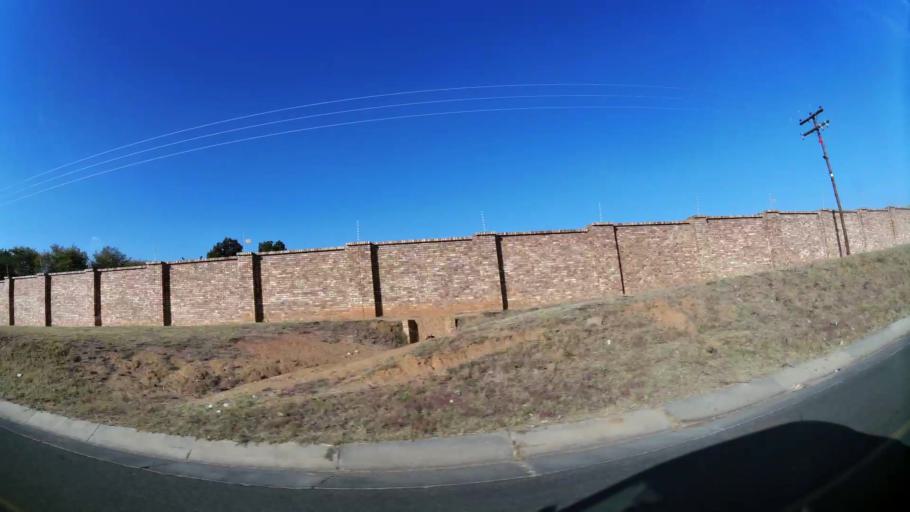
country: ZA
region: Gauteng
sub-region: West Rand District Municipality
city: Muldersdriseloop
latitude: -26.0251
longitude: 27.9085
